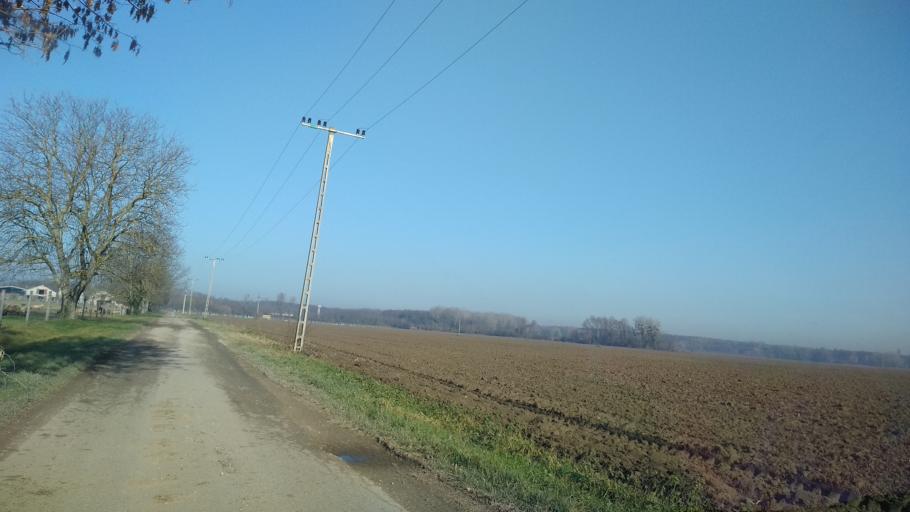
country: HU
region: Somogy
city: Barcs
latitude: 45.9487
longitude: 17.4881
